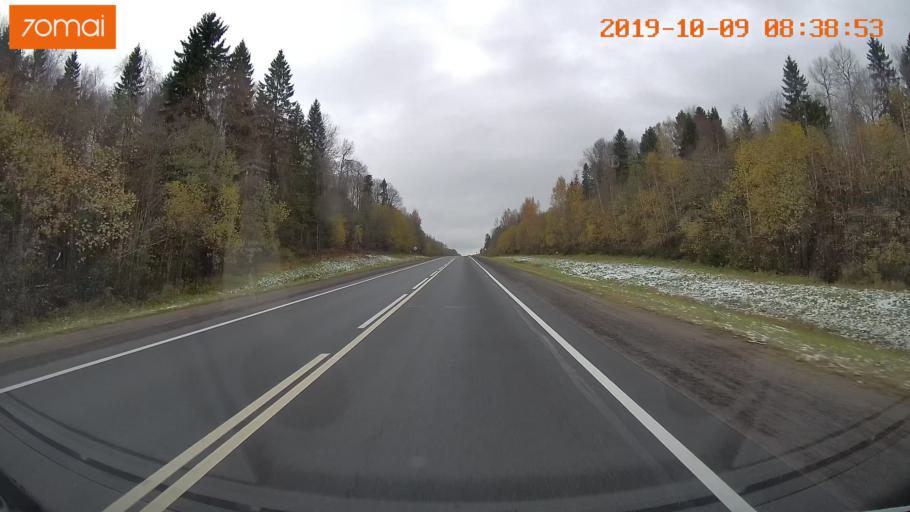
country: RU
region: Vologda
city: Gryazovets
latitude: 58.9633
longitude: 40.1600
